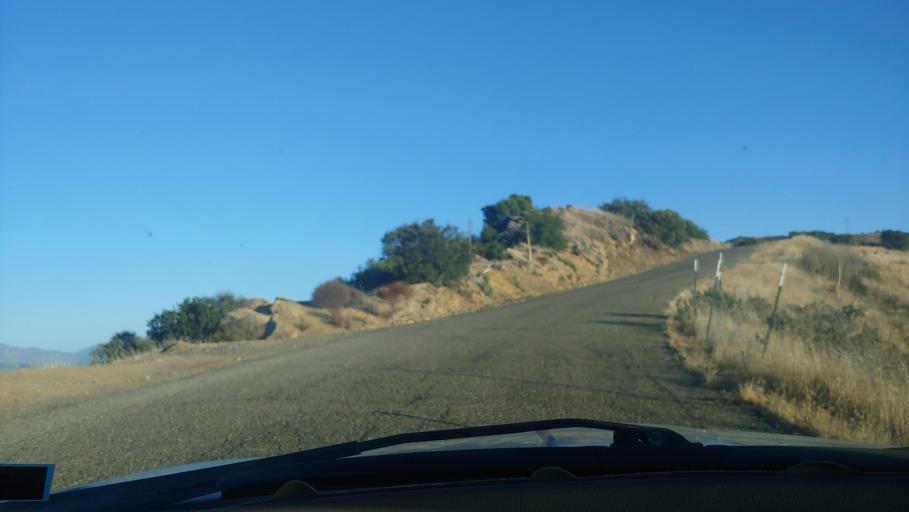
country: US
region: California
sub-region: Santa Barbara County
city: Goleta
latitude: 34.5171
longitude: -119.7801
